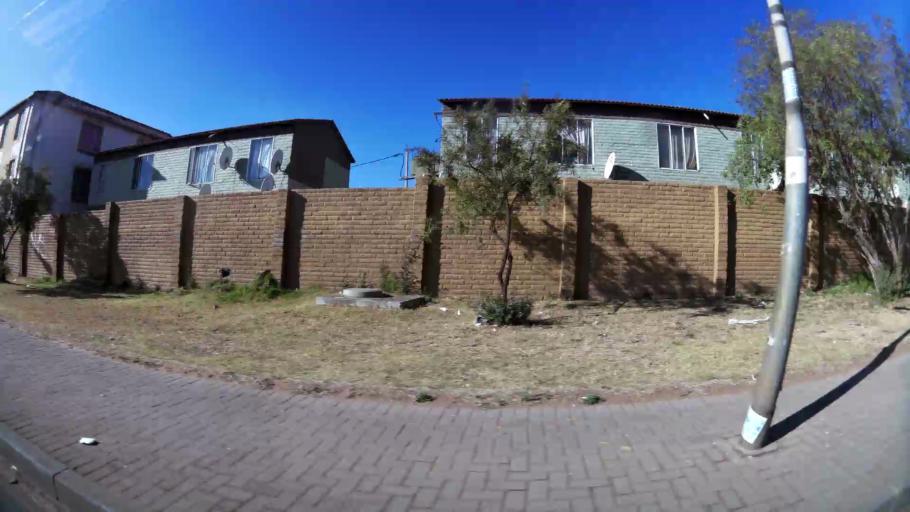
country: ZA
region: Gauteng
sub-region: City of Johannesburg Metropolitan Municipality
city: Roodepoort
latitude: -26.2153
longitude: 27.9464
